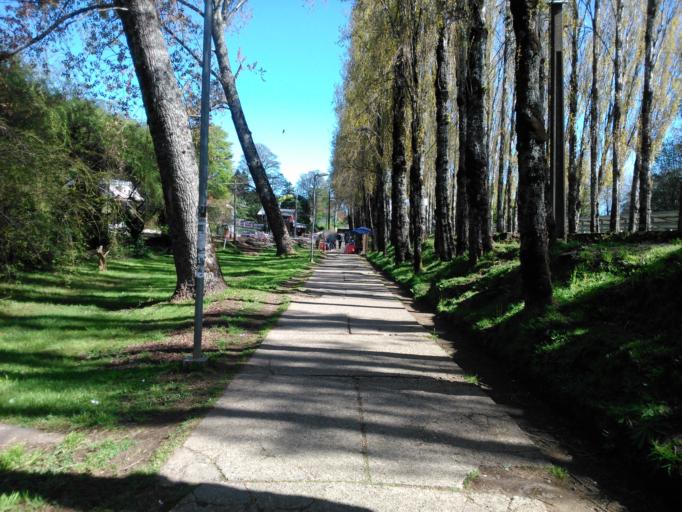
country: CL
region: Los Rios
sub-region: Provincia de Valdivia
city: Valdivia
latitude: -39.8087
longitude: -73.2514
